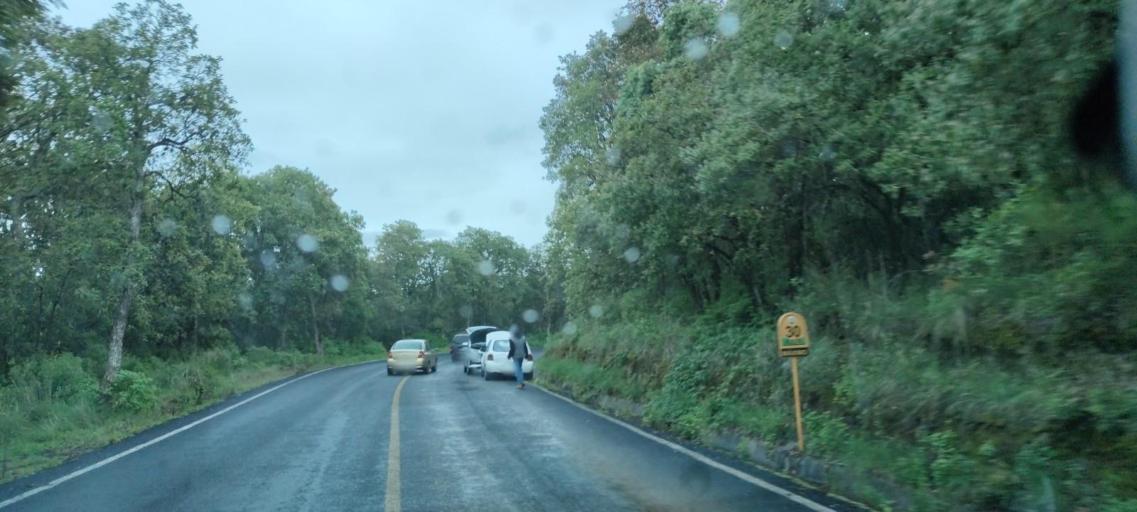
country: MX
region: Mexico
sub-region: Morelos
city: San Marcos Tlazalpan
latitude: 19.8751
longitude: -99.6611
